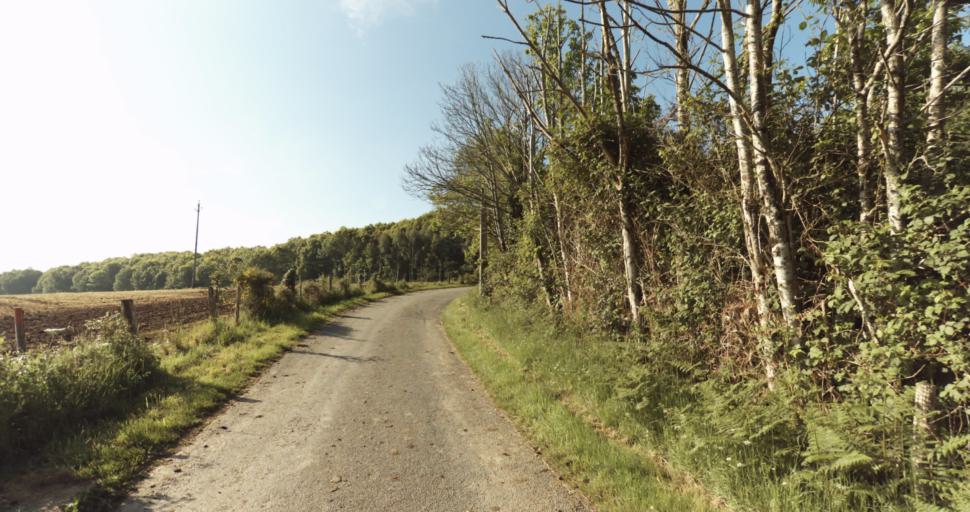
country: FR
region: Limousin
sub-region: Departement de la Haute-Vienne
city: Solignac
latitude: 45.7308
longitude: 1.2610
